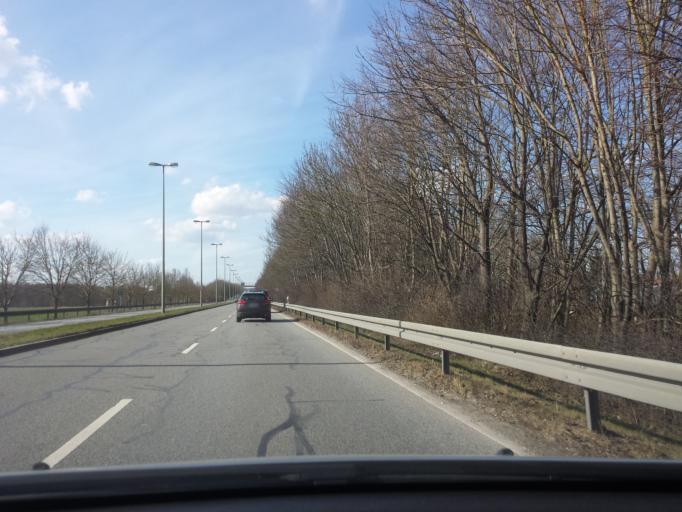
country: DE
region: Bavaria
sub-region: Upper Bavaria
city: Karlsfeld
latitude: 48.2030
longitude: 11.4904
